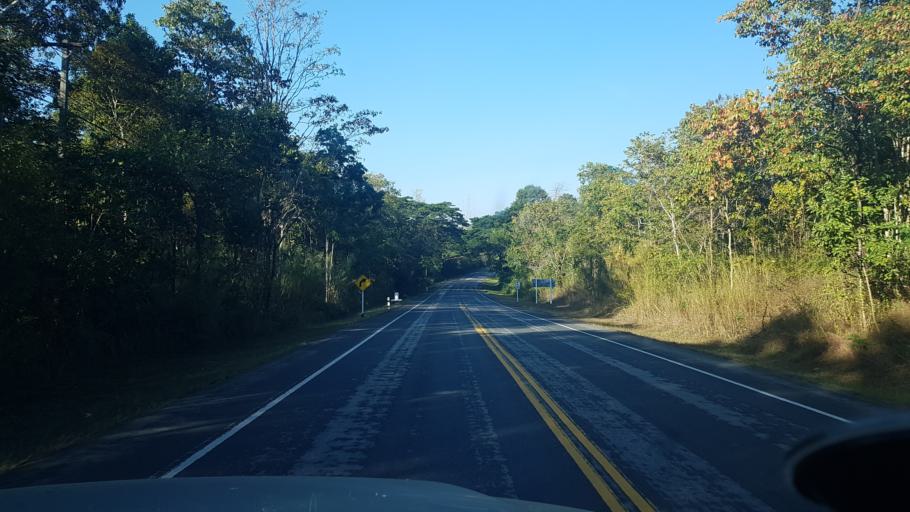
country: TH
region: Phetchabun
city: Lom Sak
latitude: 16.7365
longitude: 101.4377
